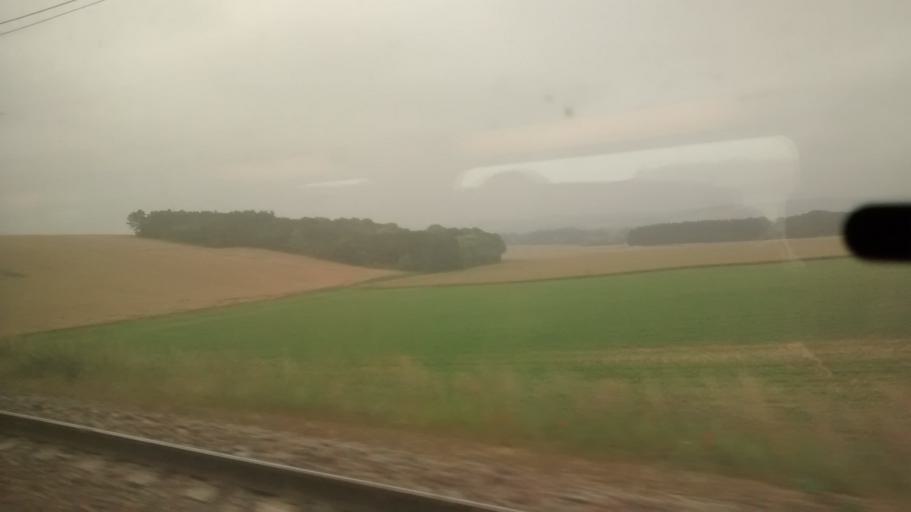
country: FR
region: Bourgogne
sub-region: Departement de l'Yonne
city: Courlon-sur-Yonne
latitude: 48.3361
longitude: 3.2053
